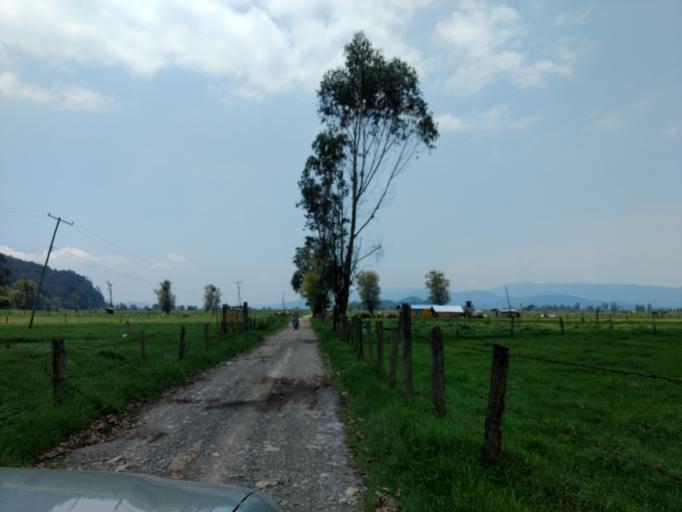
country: CO
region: Boyaca
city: Raquira
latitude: 5.5017
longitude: -73.7072
